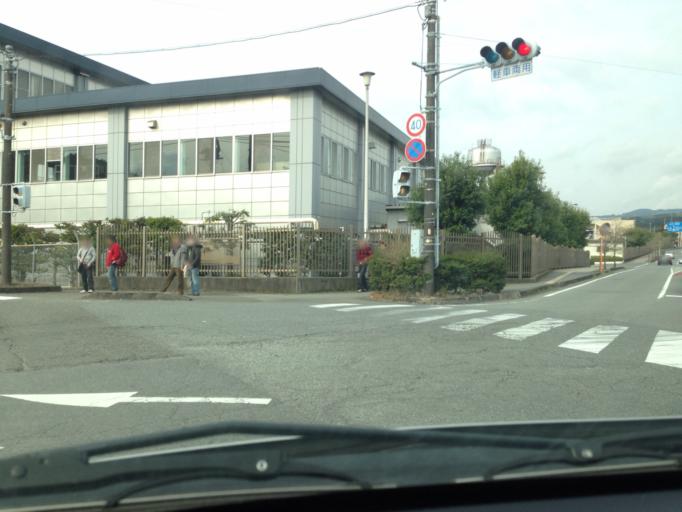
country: JP
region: Shizuoka
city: Mishima
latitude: 35.1642
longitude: 138.9106
